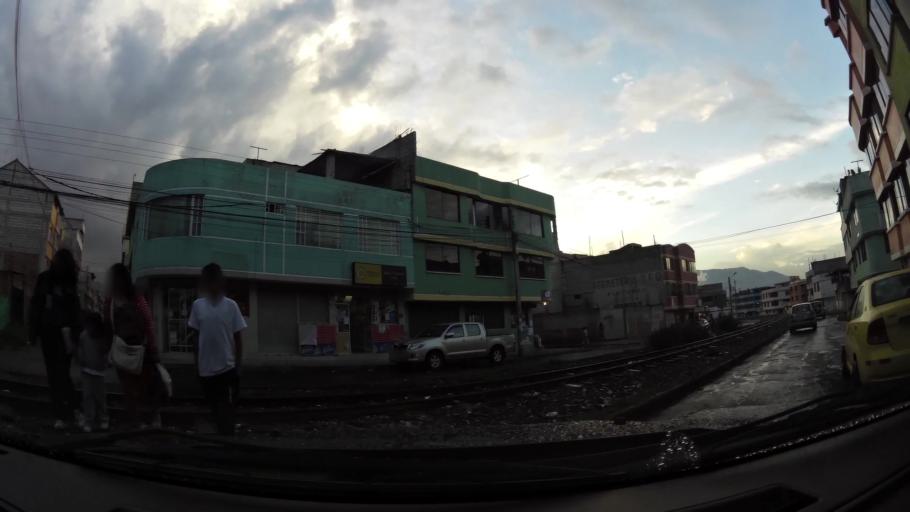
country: EC
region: Pichincha
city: Quito
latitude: -0.3022
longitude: -78.5398
